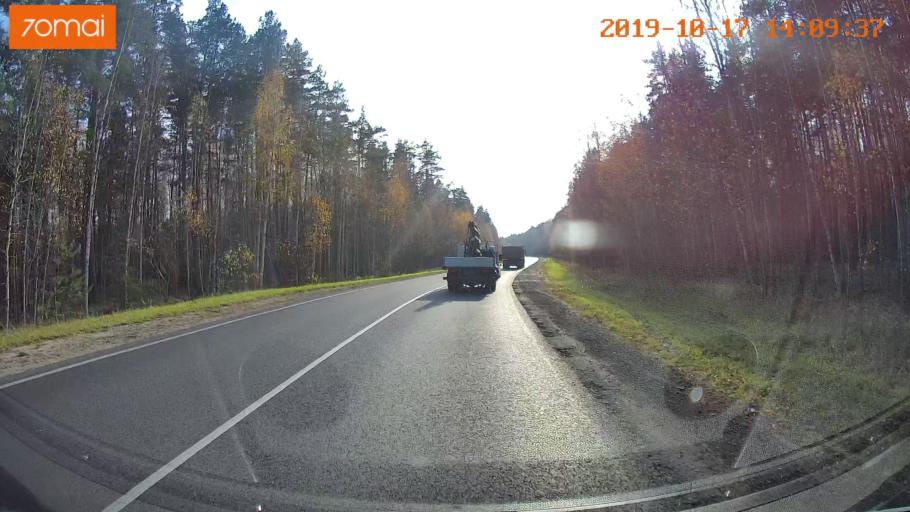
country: RU
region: Rjazan
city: Spas-Klepiki
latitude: 55.0871
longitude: 40.0562
